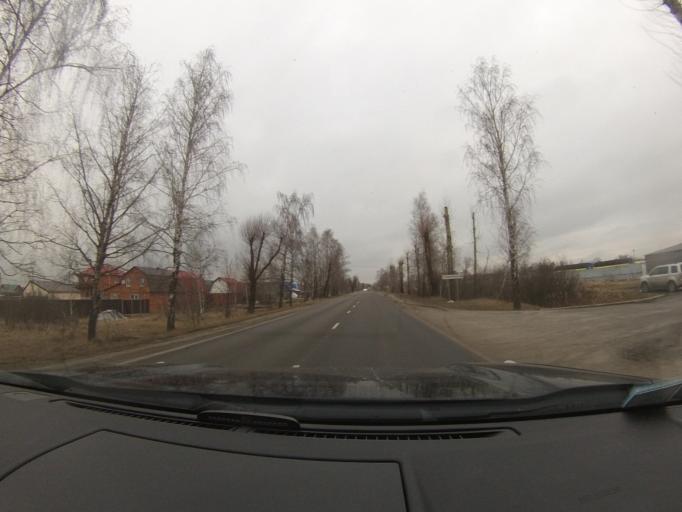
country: RU
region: Moskovskaya
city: Lopatinskiy
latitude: 55.3311
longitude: 38.7239
